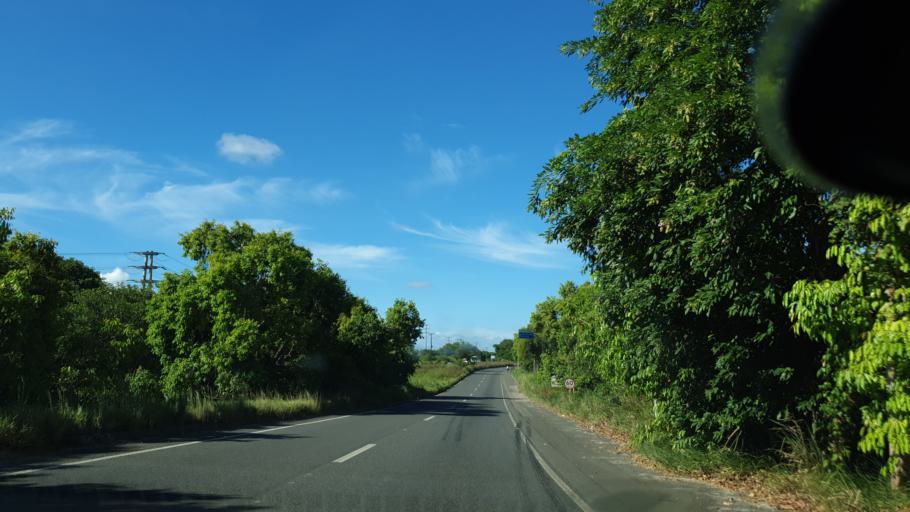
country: BR
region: Bahia
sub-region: Camacari
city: Camacari
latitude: -12.6807
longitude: -38.3022
